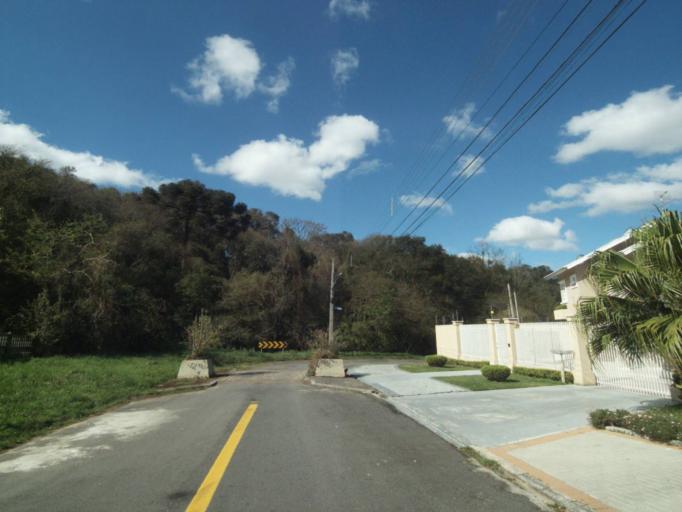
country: BR
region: Parana
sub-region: Curitiba
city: Curitiba
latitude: -25.3794
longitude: -49.2520
